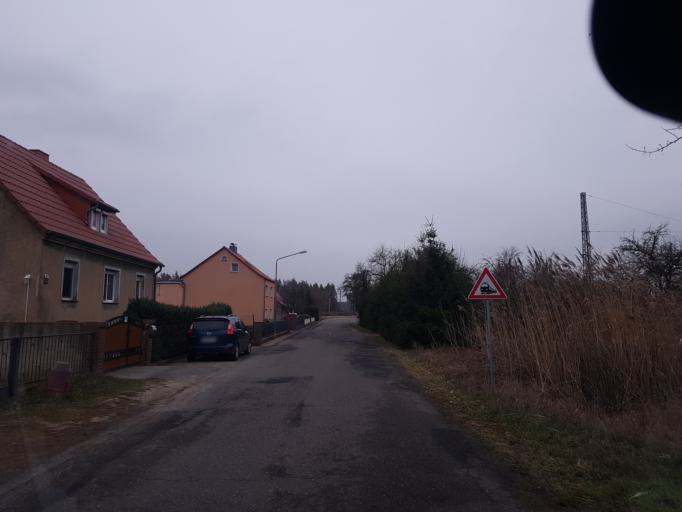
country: DE
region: Brandenburg
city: Falkenberg
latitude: 51.5760
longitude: 13.2541
